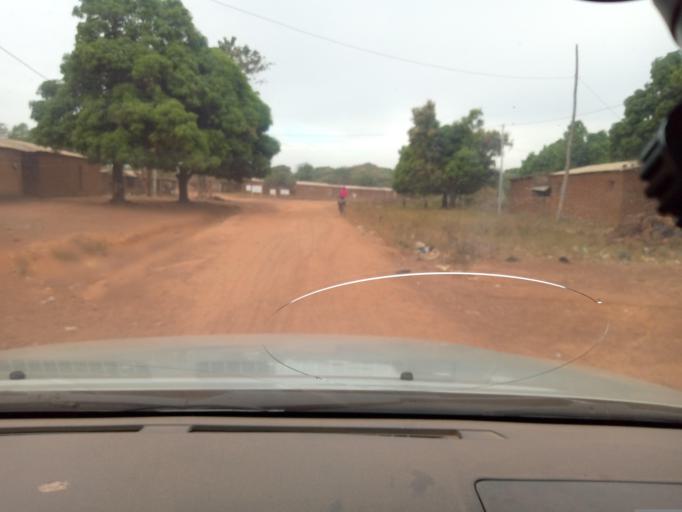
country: ML
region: Sikasso
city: Sikasso
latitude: 10.9695
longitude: -5.6872
